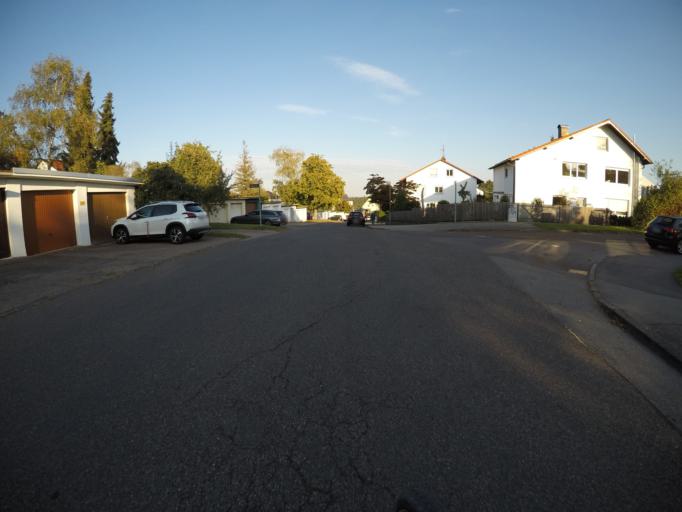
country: DE
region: Baden-Wuerttemberg
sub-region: Regierungsbezirk Stuttgart
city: Ostfildern
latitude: 48.7422
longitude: 9.2333
